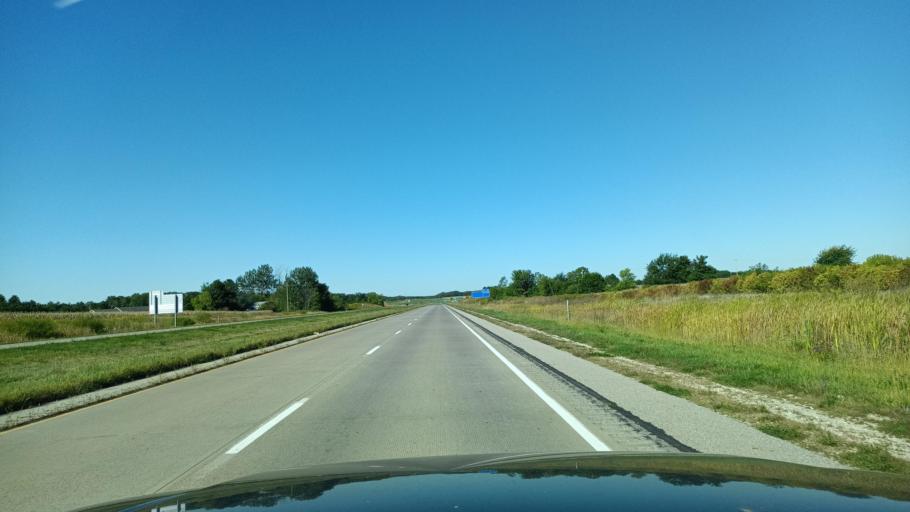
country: US
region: Iowa
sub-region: Lee County
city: Fort Madison
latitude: 40.6706
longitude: -91.3410
